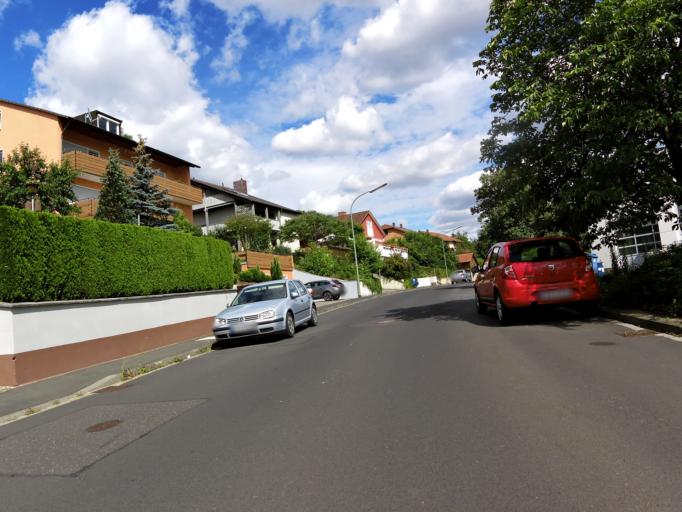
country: DE
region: Bavaria
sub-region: Regierungsbezirk Unterfranken
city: Zell am Main
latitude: 49.8150
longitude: 9.8872
